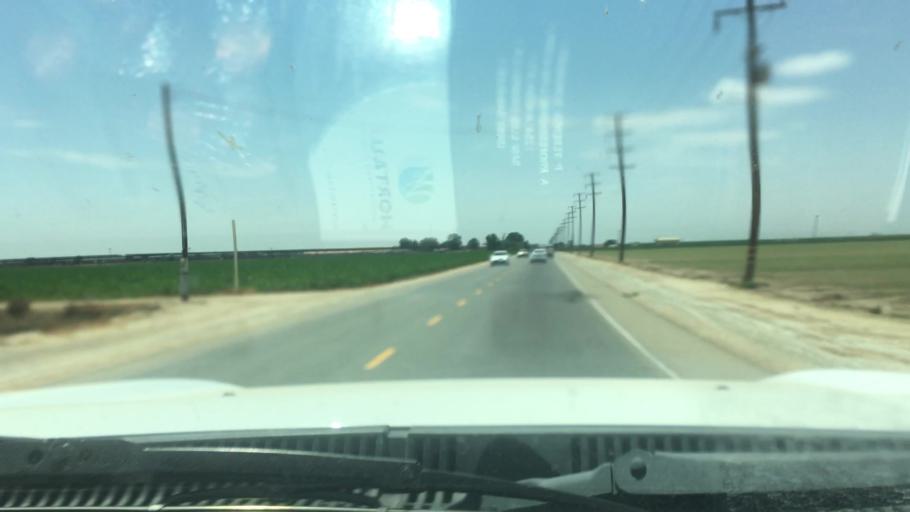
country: US
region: California
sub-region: Tulare County
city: Tipton
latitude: 36.0657
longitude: -119.2814
